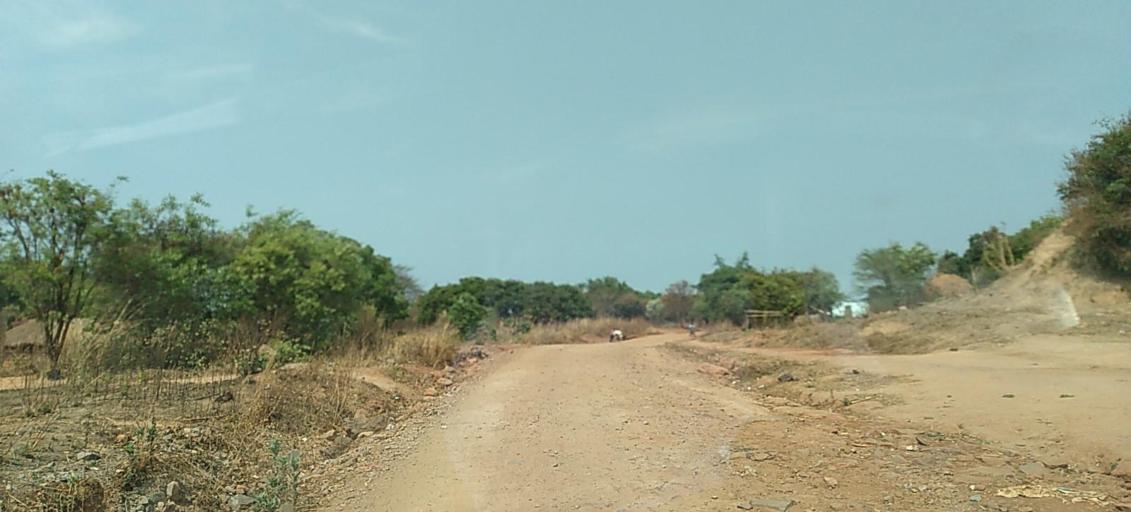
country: ZM
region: Copperbelt
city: Chililabombwe
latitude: -12.3411
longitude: 27.7117
